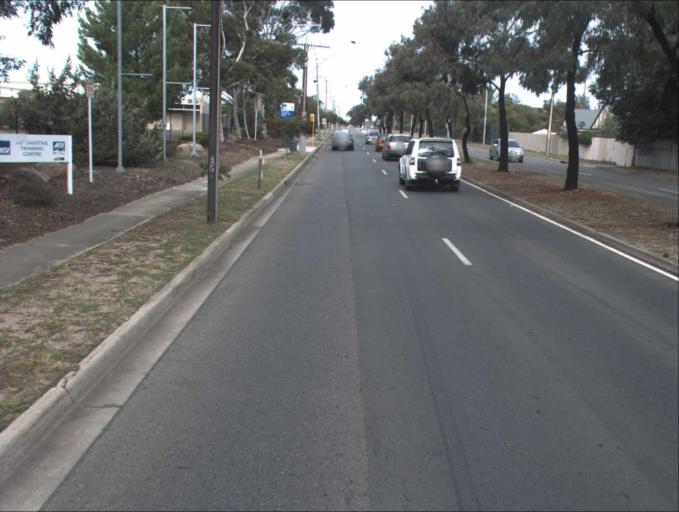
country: AU
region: South Australia
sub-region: Charles Sturt
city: West Lakes Shore
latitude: -34.8619
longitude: 138.5023
